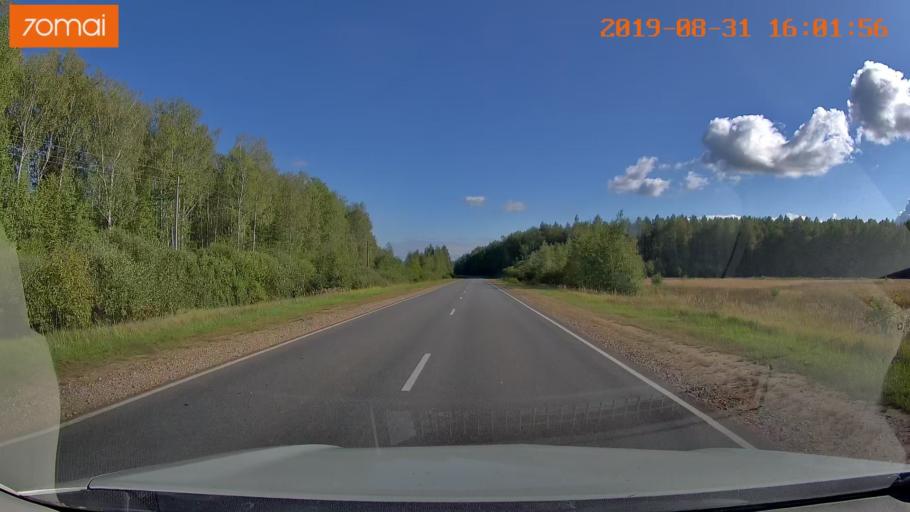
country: RU
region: Kaluga
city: Yukhnov
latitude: 54.6821
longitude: 35.2954
